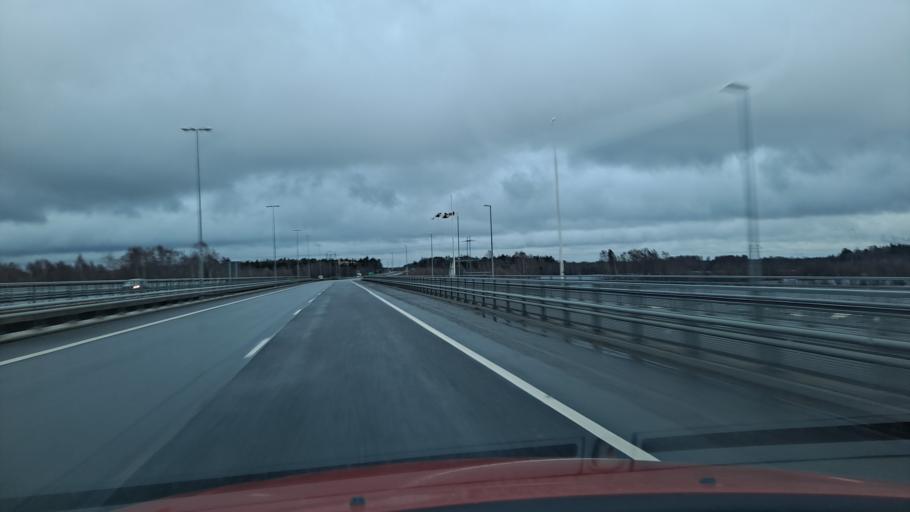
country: FI
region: Lapland
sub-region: Kemi-Tornio
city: Keminmaa
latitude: 65.7882
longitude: 24.5340
